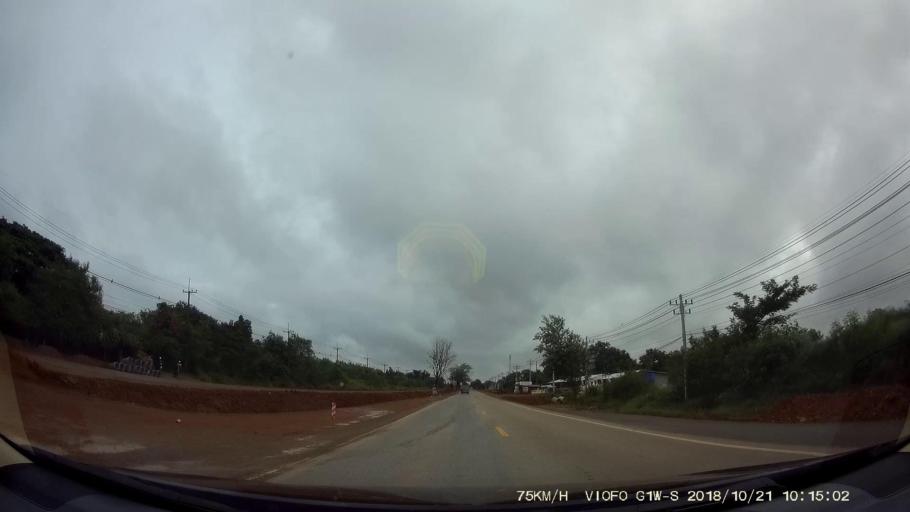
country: TH
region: Chaiyaphum
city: Phu Khiao
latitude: 16.3442
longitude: 102.1617
